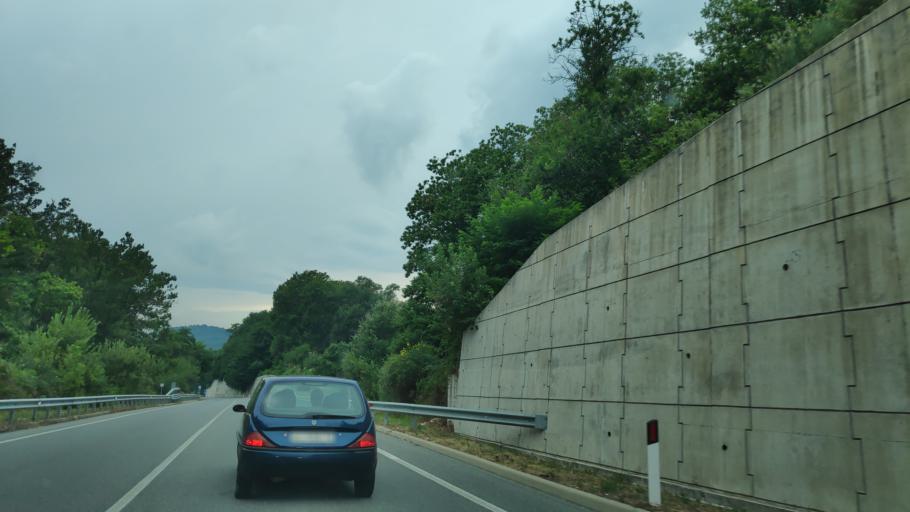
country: IT
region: Calabria
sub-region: Provincia di Catanzaro
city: Chiaravalle Centrale
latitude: 38.6667
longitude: 16.3987
